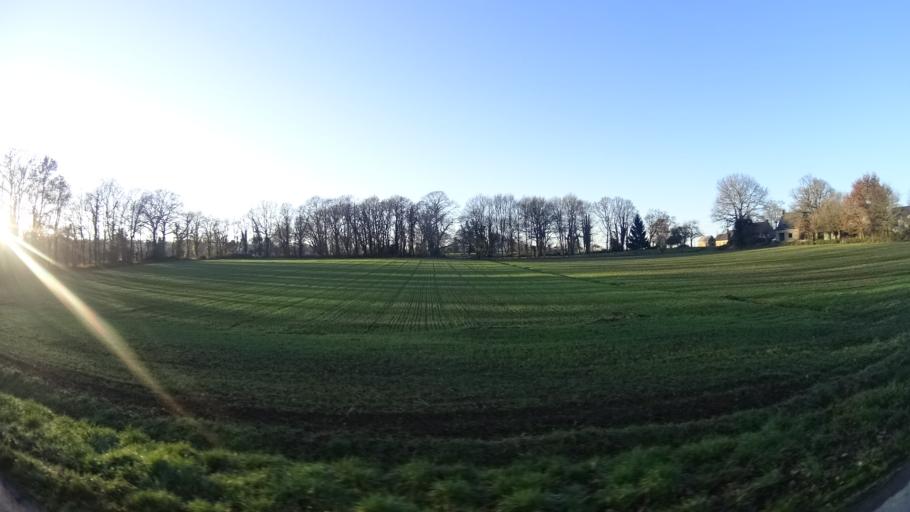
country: FR
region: Brittany
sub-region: Departement du Morbihan
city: Saint-Jean-la-Poterie
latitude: 47.6541
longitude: -2.1213
